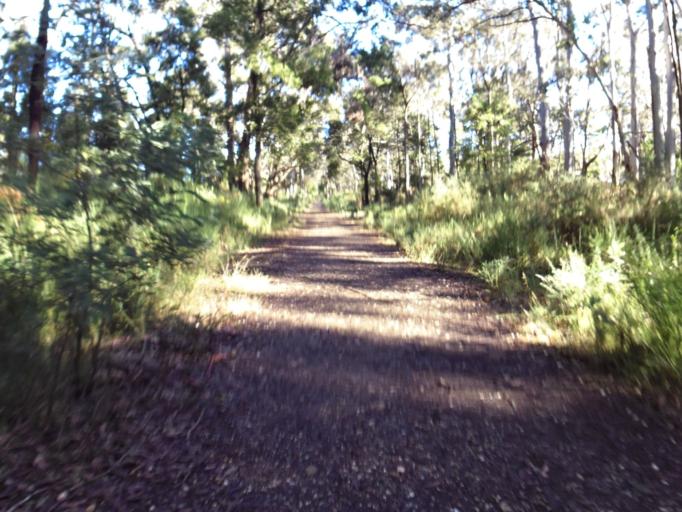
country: AU
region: Victoria
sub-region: Moorabool
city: Bacchus Marsh
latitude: -37.3885
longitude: 144.3018
